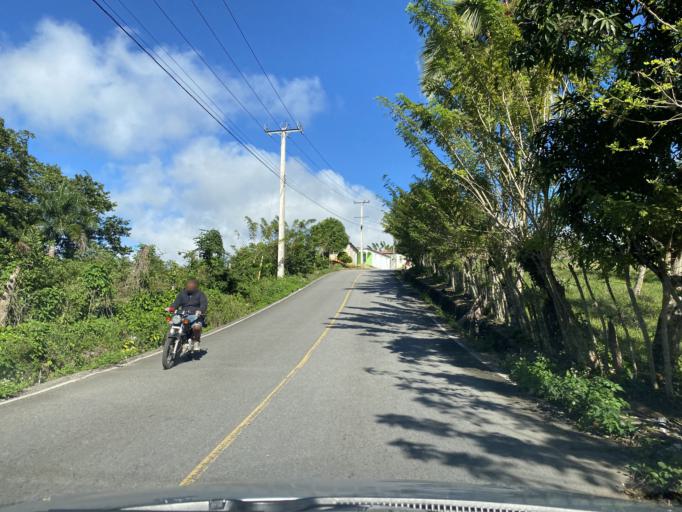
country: DO
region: Samana
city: Sanchez
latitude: 19.2510
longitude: -69.5888
